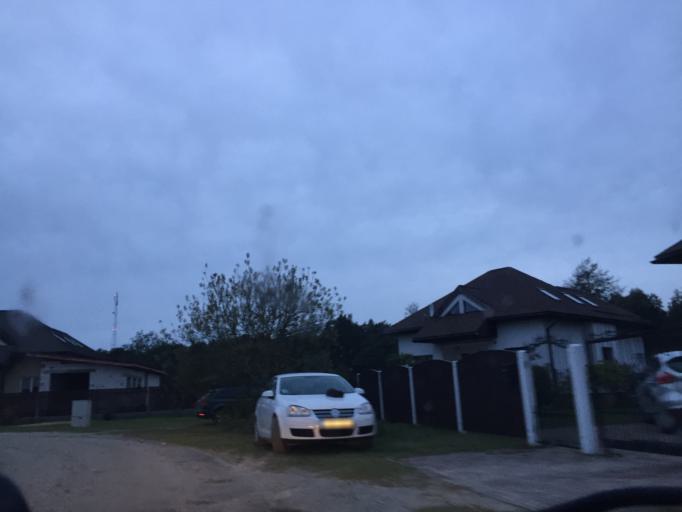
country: LV
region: Adazi
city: Adazi
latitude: 57.0896
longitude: 24.3746
